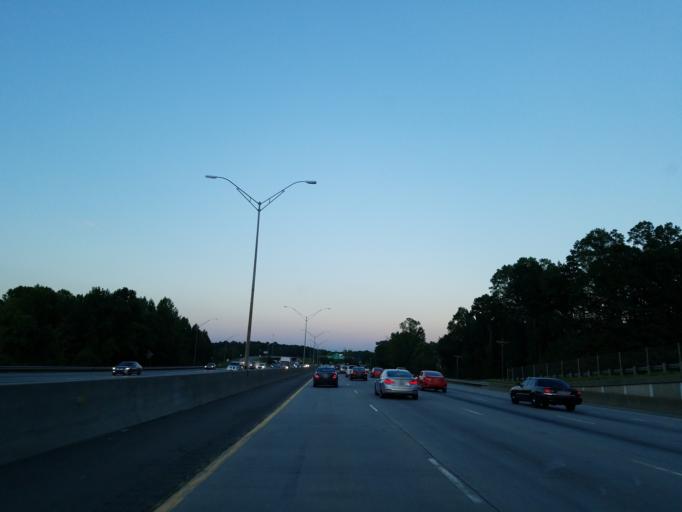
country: US
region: North Carolina
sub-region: Mecklenburg County
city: Charlotte
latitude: 35.2817
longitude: -80.7826
